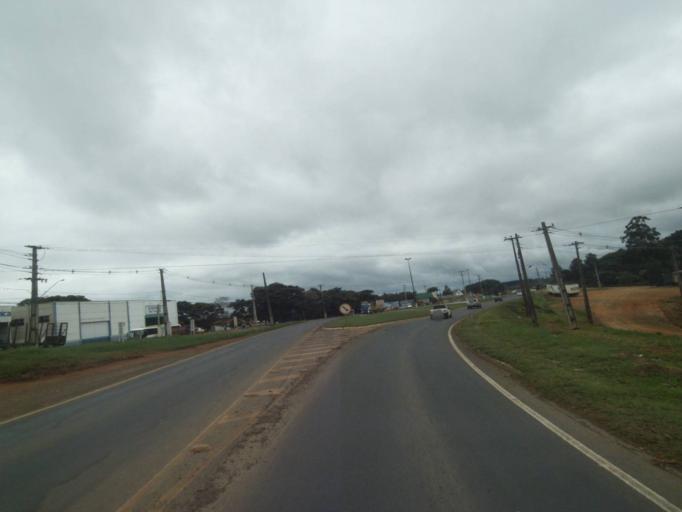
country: BR
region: Parana
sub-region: Telemaco Borba
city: Telemaco Borba
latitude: -24.3476
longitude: -50.6611
